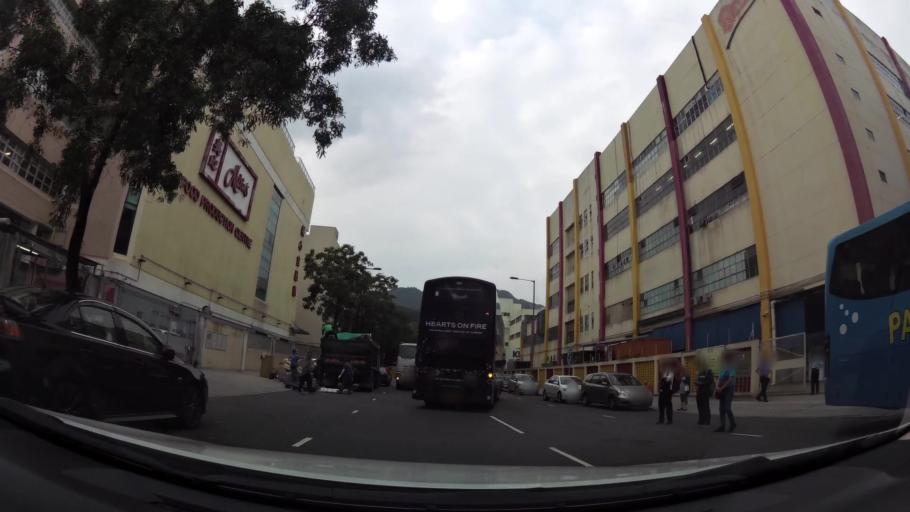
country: HK
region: Tai Po
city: Tai Po
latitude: 22.4594
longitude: 114.1848
